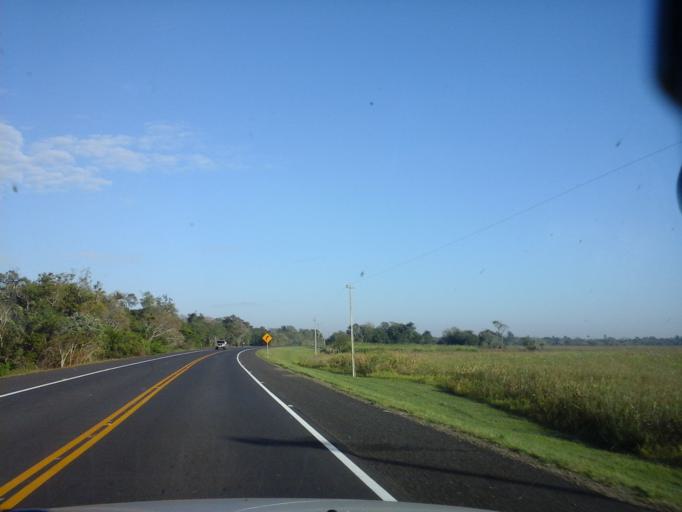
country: PY
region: Neembucu
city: Pilar
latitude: -26.8766
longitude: -57.8932
